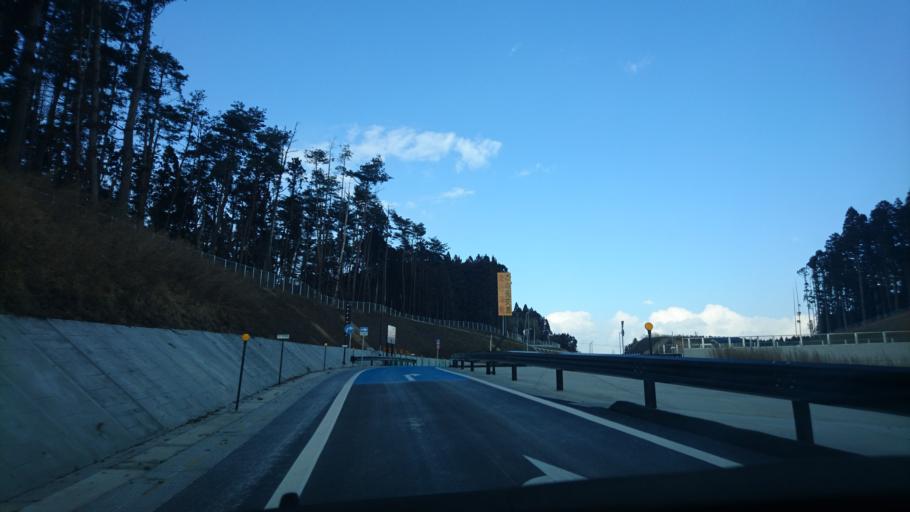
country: JP
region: Iwate
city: Ofunato
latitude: 38.8033
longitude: 141.5380
